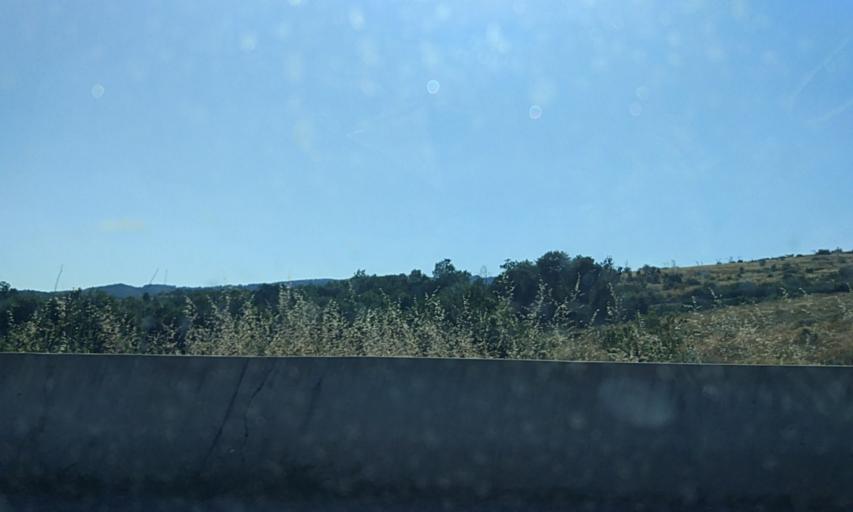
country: PT
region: Braganca
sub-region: Braganca Municipality
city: Braganca
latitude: 41.6798
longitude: -6.8177
